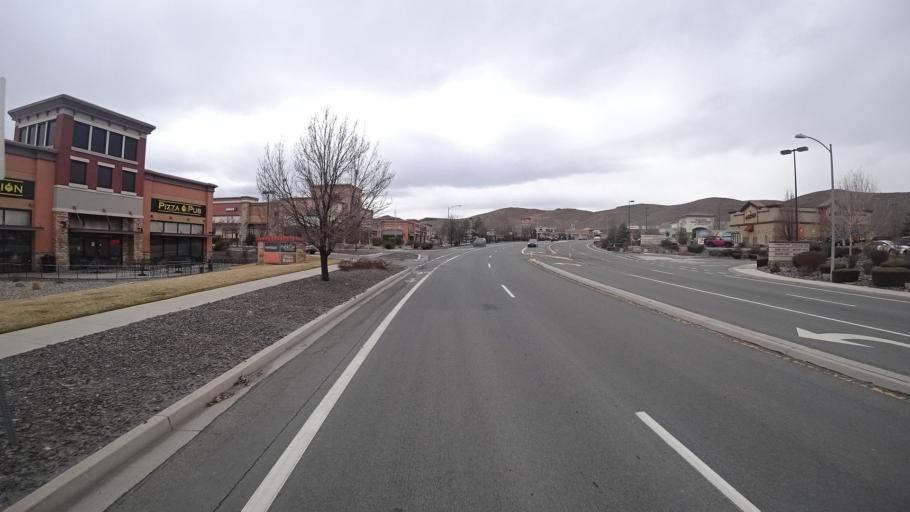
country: US
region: Nevada
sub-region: Washoe County
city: Sun Valley
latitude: 39.5834
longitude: -119.7402
